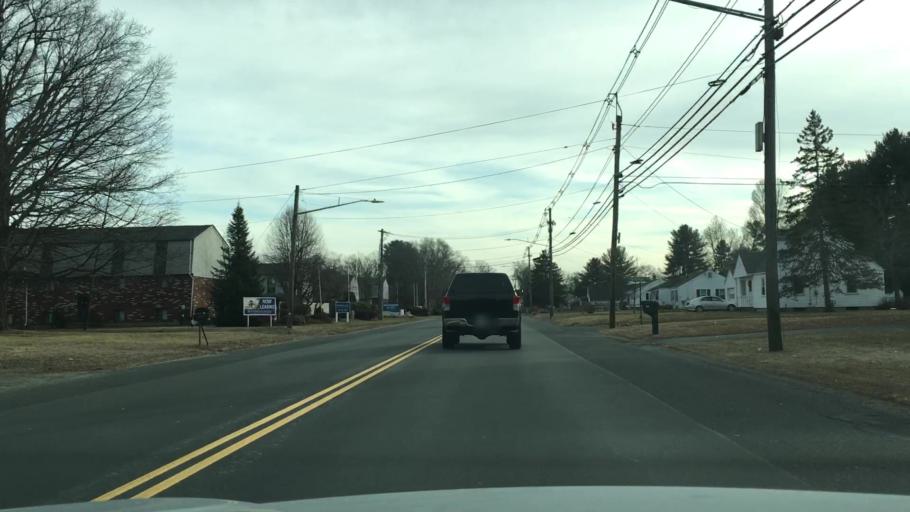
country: US
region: Massachusetts
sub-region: Hampden County
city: Westfield
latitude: 42.1012
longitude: -72.7639
